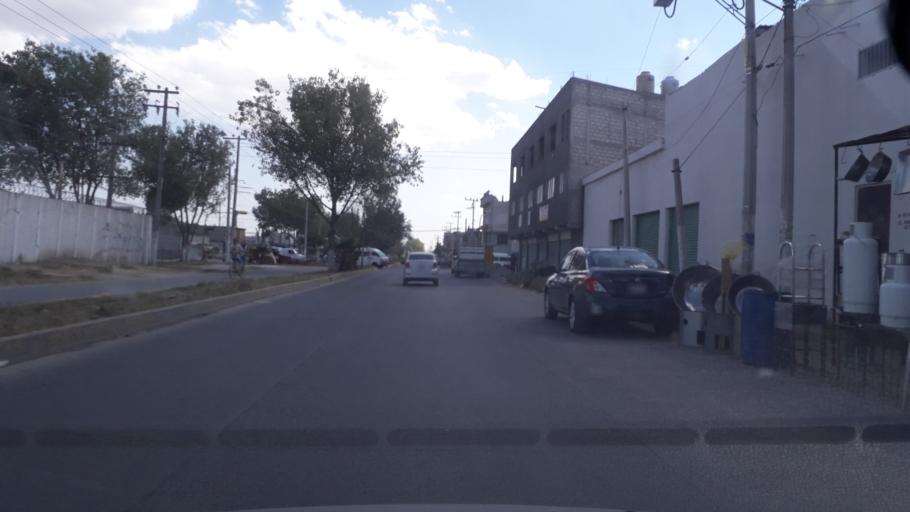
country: MX
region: Mexico
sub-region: Jaltenco
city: Alborada Jaltenco
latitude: 19.6462
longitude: -99.0619
